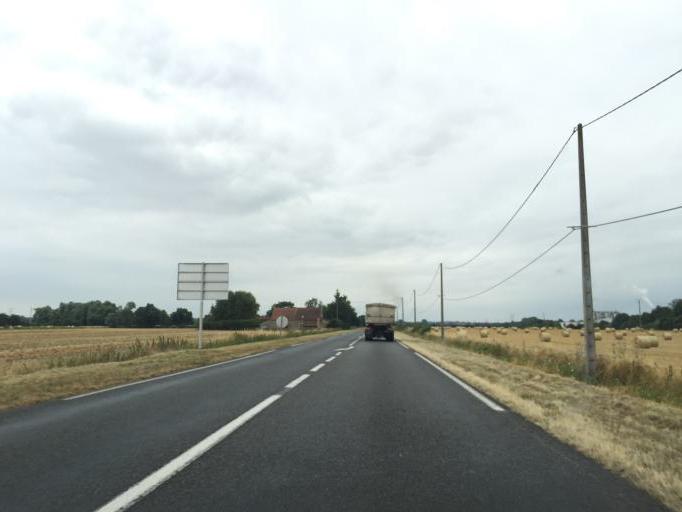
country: FR
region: Auvergne
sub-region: Departement de l'Allier
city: Saint-Pourcain-sur-Sioule
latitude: 46.2634
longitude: 3.2889
